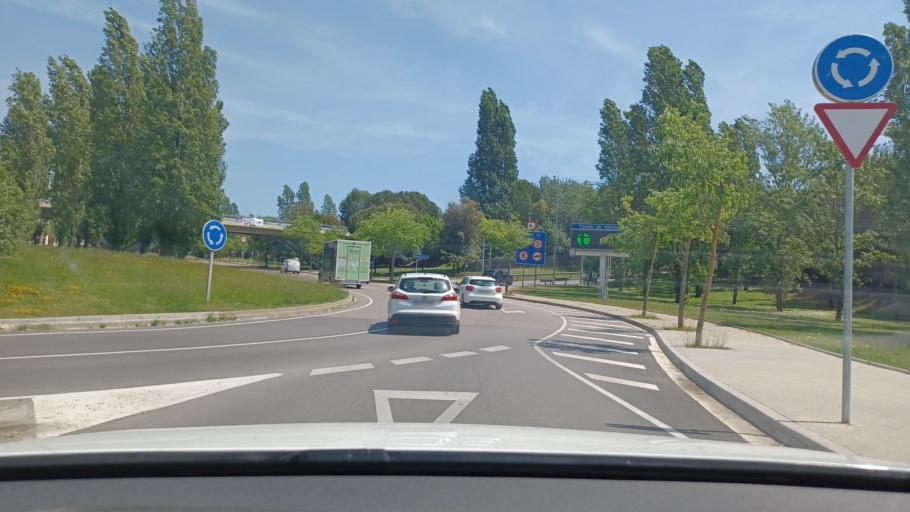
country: ES
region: Catalonia
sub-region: Provincia de Barcelona
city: Sant Cugat del Valles
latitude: 41.4791
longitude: 2.0644
